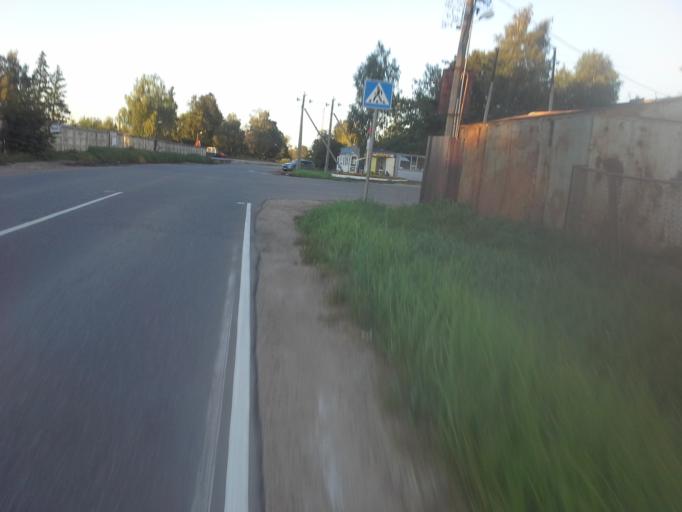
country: RU
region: Moskovskaya
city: Selyatino
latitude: 55.5245
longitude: 36.9683
